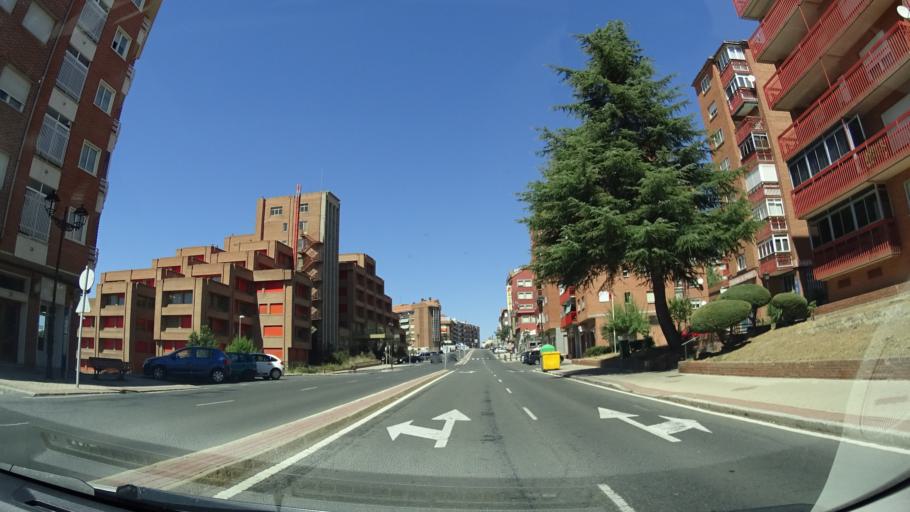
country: ES
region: Castille and Leon
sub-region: Provincia de Avila
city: Avila
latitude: 40.6526
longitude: -4.6819
